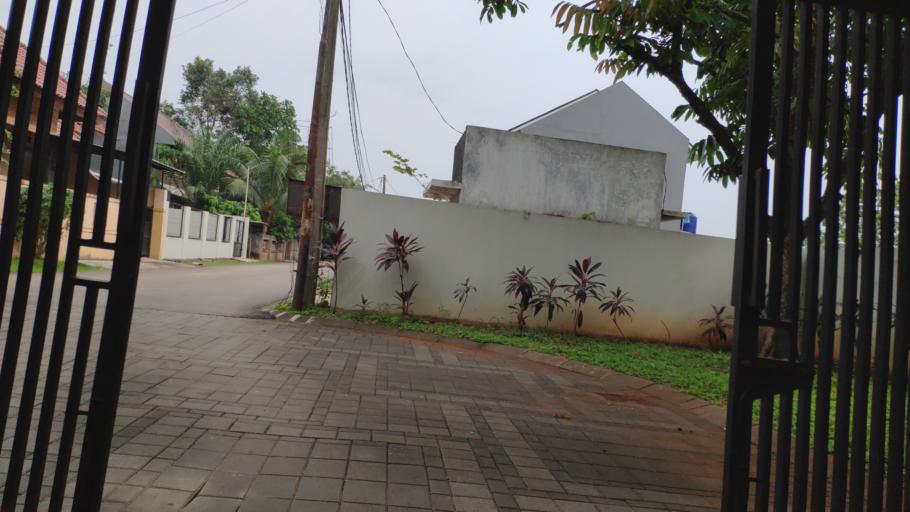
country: ID
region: West Java
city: Depok
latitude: -6.3535
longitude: 106.7953
